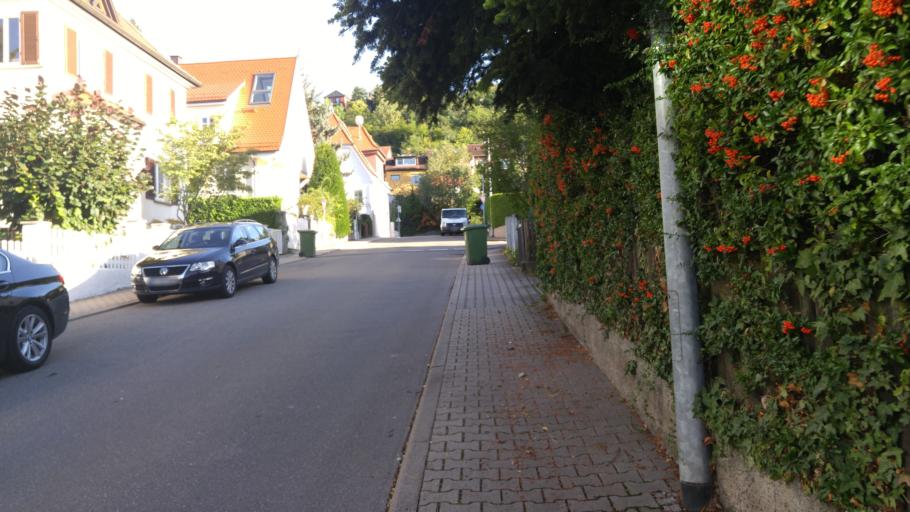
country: DE
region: Baden-Wuerttemberg
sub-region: Regierungsbezirk Stuttgart
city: Gerlingen
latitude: 48.7952
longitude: 9.0636
